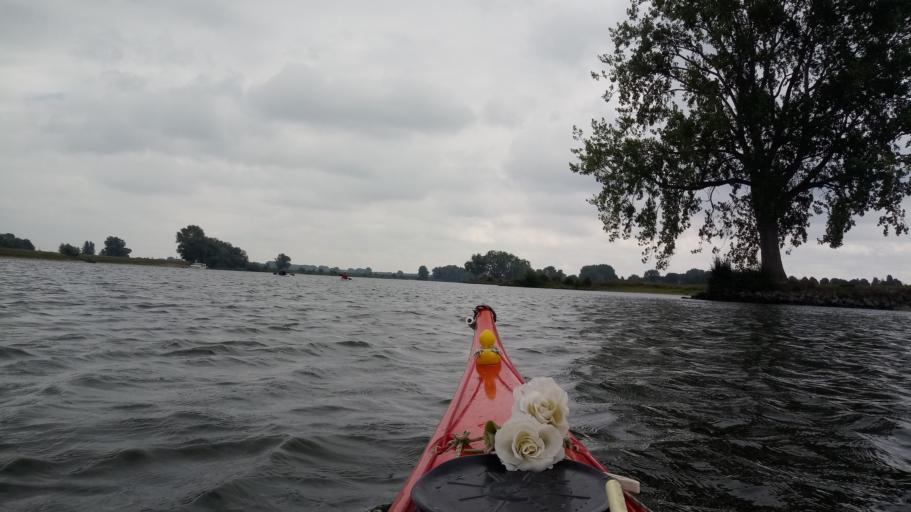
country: NL
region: Gelderland
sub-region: Gemeente Maasdriel
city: Hedel
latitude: 51.7426
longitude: 5.2248
